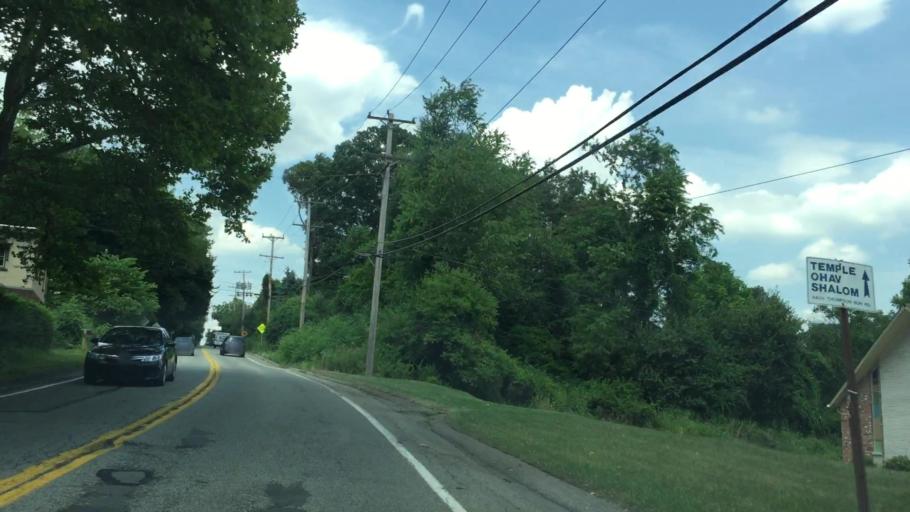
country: US
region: Pennsylvania
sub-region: Allegheny County
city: Allison Park
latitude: 40.5678
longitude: -79.9835
